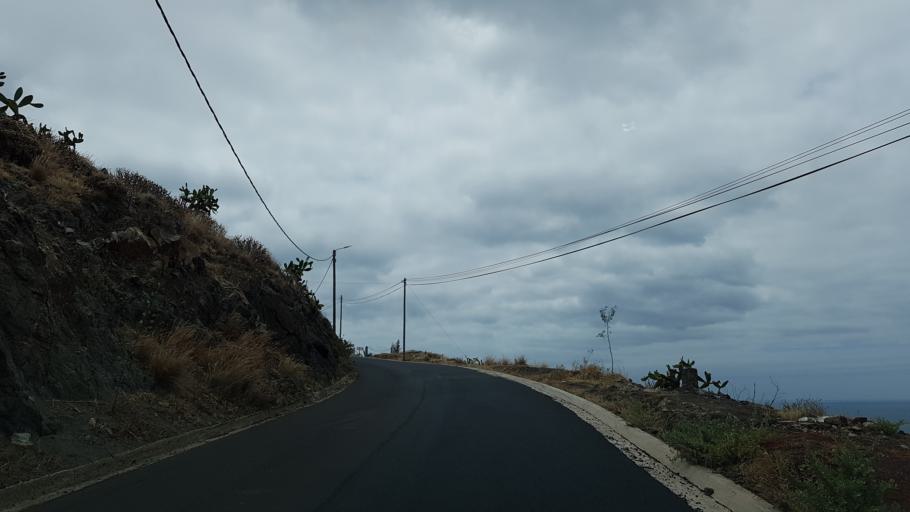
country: PT
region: Madeira
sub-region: Porto Santo
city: Vila de Porto Santo
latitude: 33.0697
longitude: -16.3217
